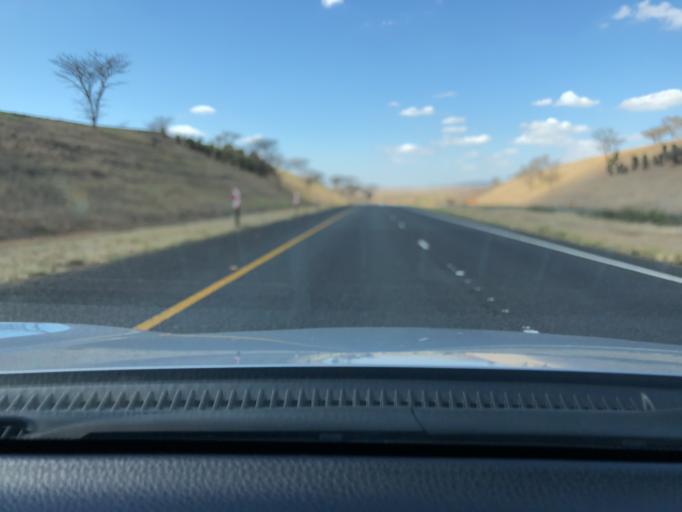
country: ZA
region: KwaZulu-Natal
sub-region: uThukela District Municipality
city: Ladysmith
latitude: -28.7482
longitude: 29.6591
